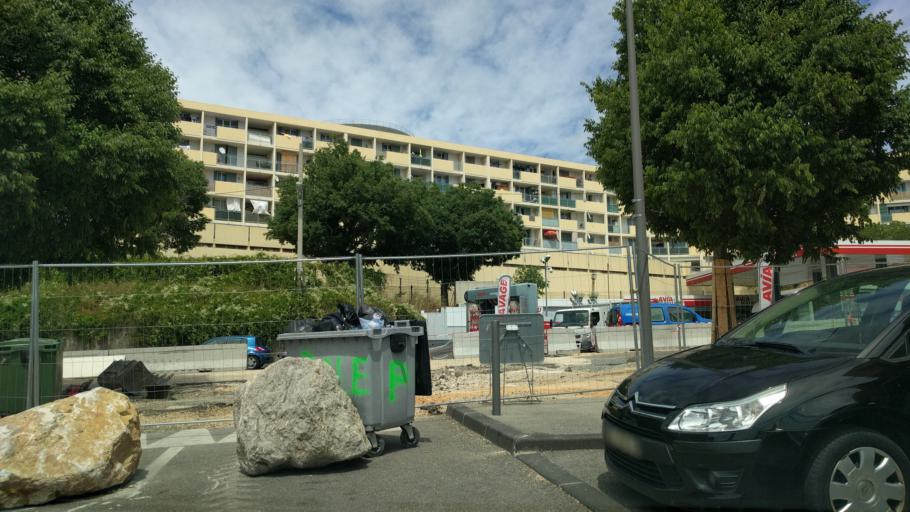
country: FR
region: Provence-Alpes-Cote d'Azur
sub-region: Departement des Bouches-du-Rhone
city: Marseille 13
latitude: 43.3339
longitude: 5.4018
